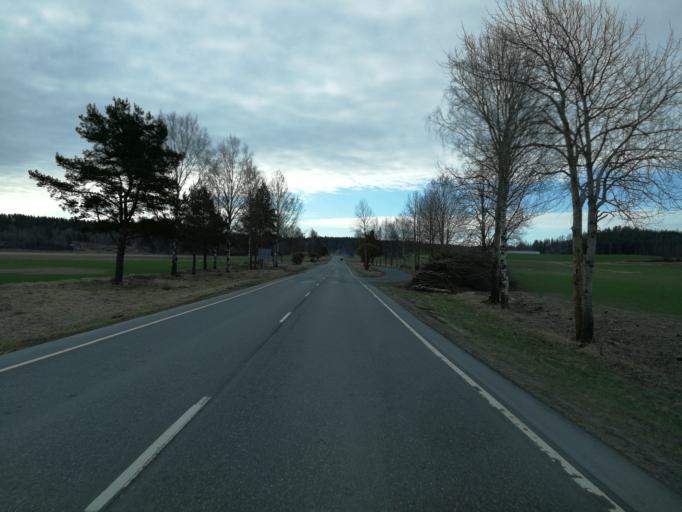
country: FI
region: Varsinais-Suomi
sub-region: Salo
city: Muurla
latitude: 60.3783
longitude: 23.3026
